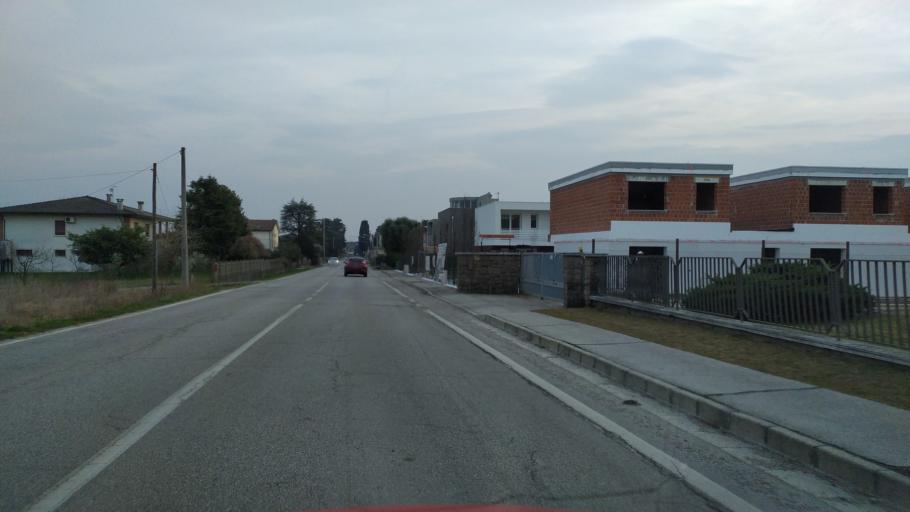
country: IT
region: Veneto
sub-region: Provincia di Vicenza
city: Montecchio Precalcino
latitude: 45.6698
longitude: 11.5628
